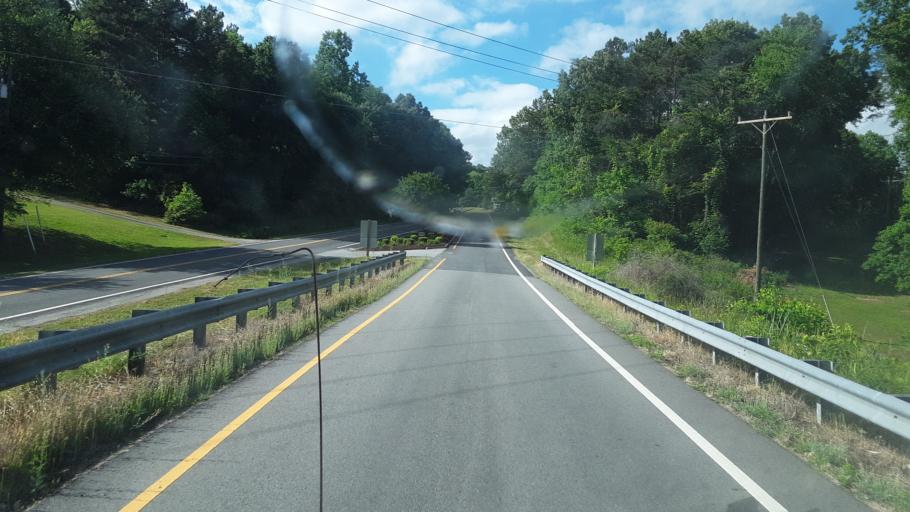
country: US
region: Virginia
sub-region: Pittsylvania County
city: Chatham
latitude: 36.8079
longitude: -79.3928
